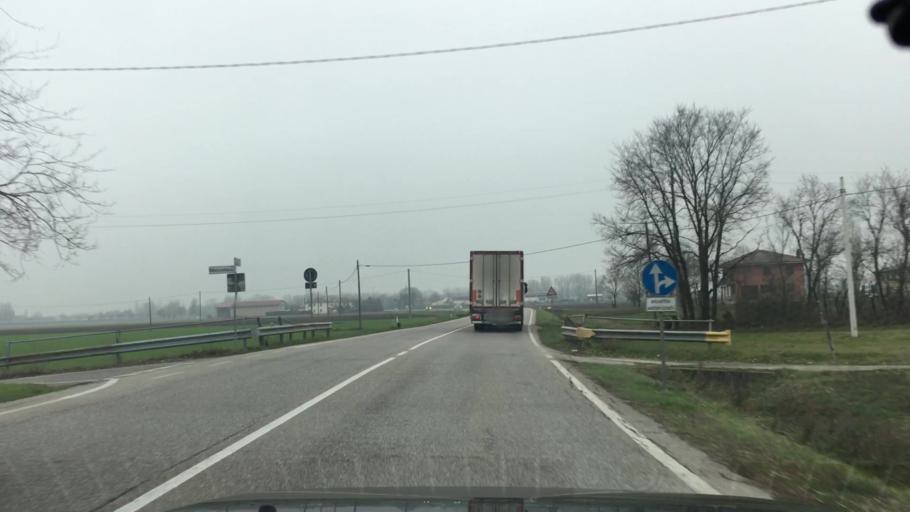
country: IT
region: Emilia-Romagna
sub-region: Provincia di Bologna
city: San Giovanni in Persiceto
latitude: 44.6256
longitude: 11.2182
